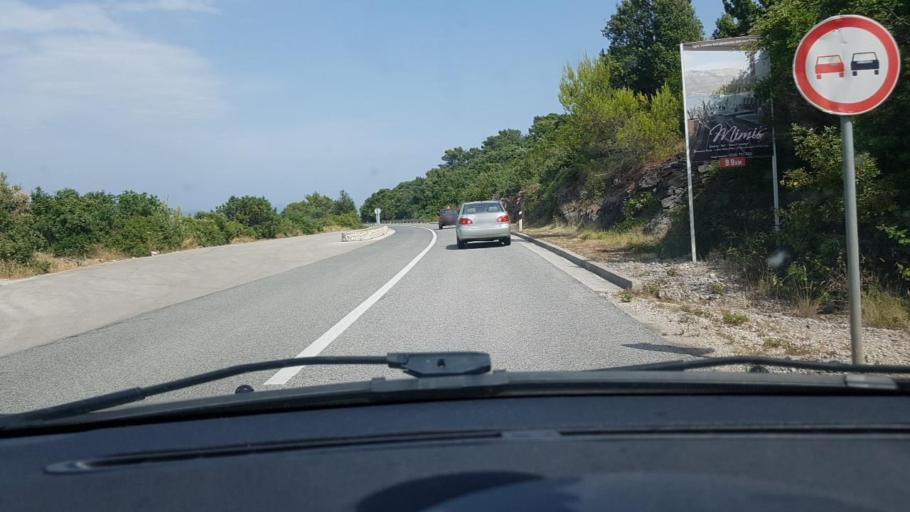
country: HR
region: Dubrovacko-Neretvanska
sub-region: Grad Korcula
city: Zrnovo
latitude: 42.9395
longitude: 17.0702
